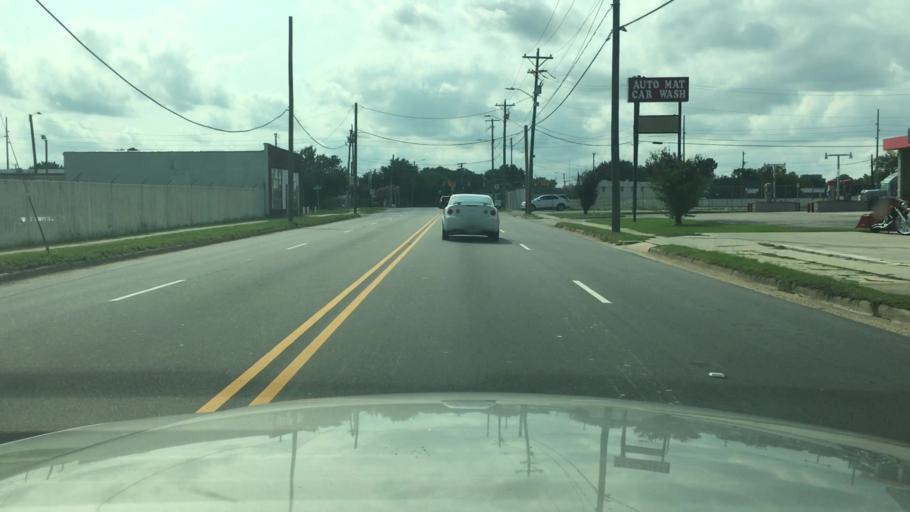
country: US
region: North Carolina
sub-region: Cumberland County
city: Fayetteville
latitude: 35.0477
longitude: -78.8629
